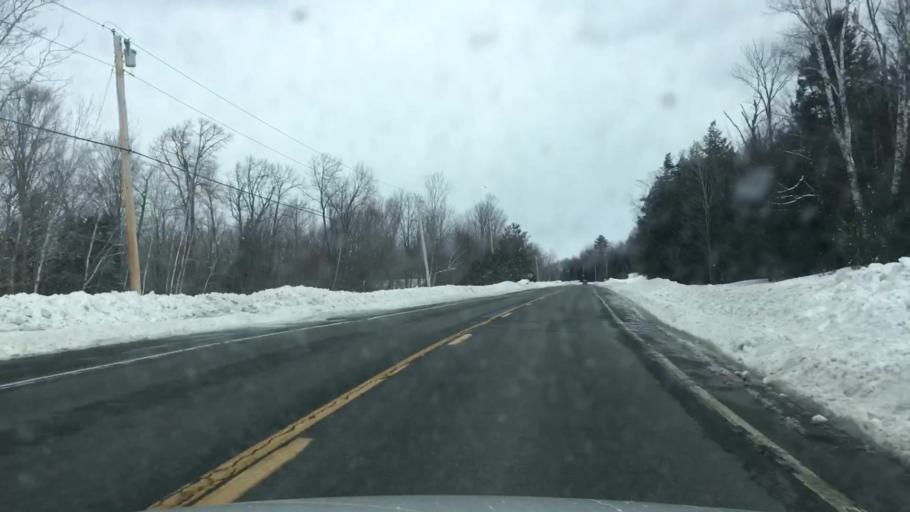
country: US
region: Maine
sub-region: Somerset County
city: Cornville
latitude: 44.8184
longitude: -69.7060
